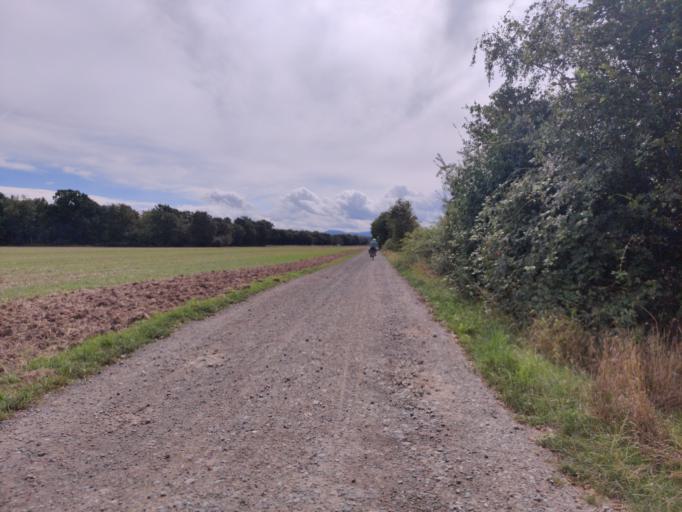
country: DE
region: Lower Saxony
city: Langelsheim
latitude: 51.9890
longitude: 10.3699
